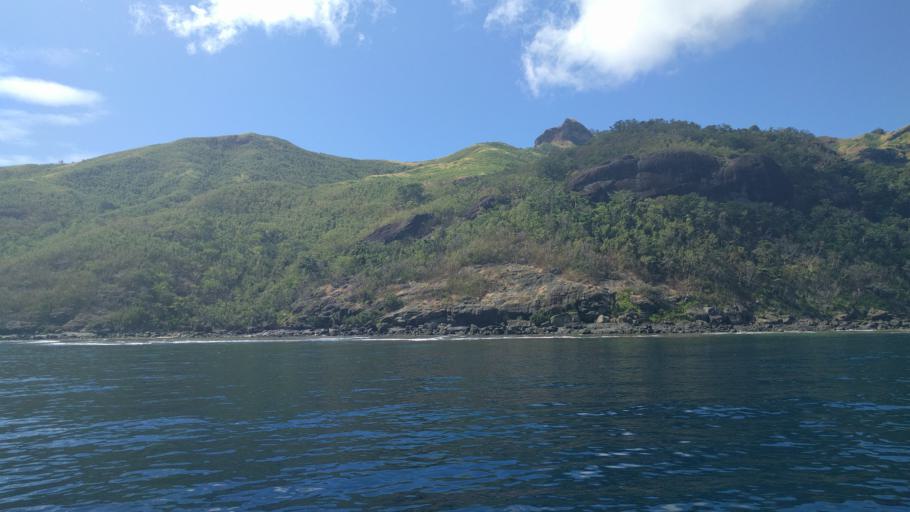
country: FJ
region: Western
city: Lautoka
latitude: -17.2873
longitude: 177.1012
